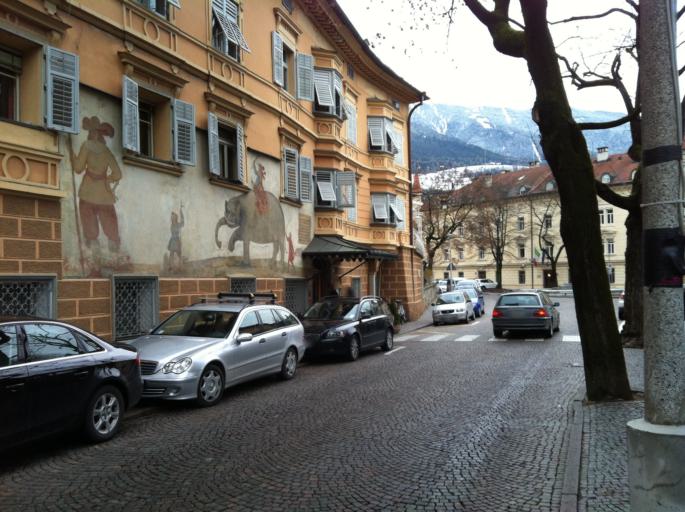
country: IT
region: Trentino-Alto Adige
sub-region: Bolzano
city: Bressanone
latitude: 46.7194
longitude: 11.6533
